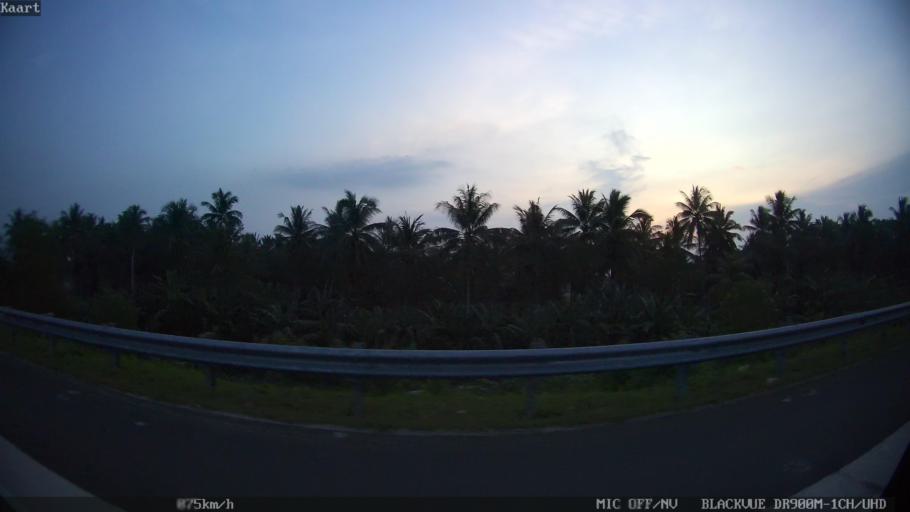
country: ID
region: Lampung
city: Kalianda
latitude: -5.6606
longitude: 105.5906
